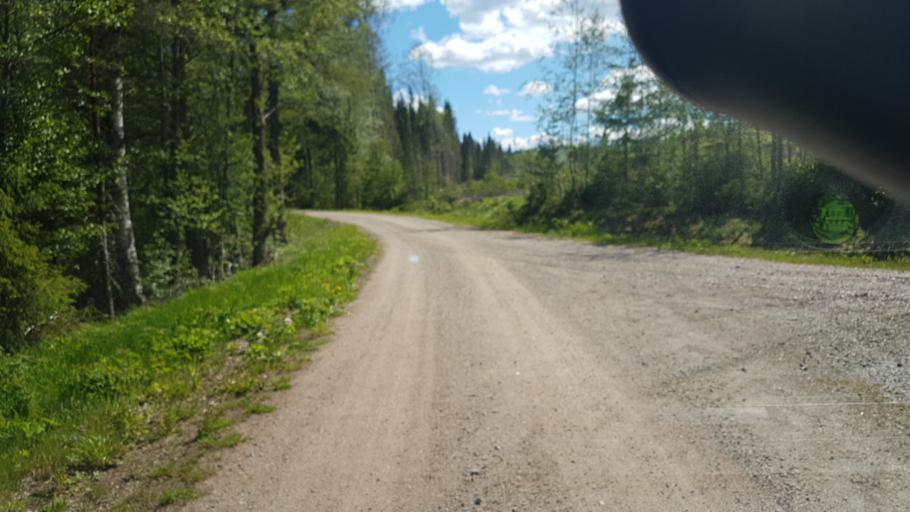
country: SE
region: Vaermland
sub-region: Karlstads Kommun
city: Edsvalla
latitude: 59.6106
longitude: 12.9824
